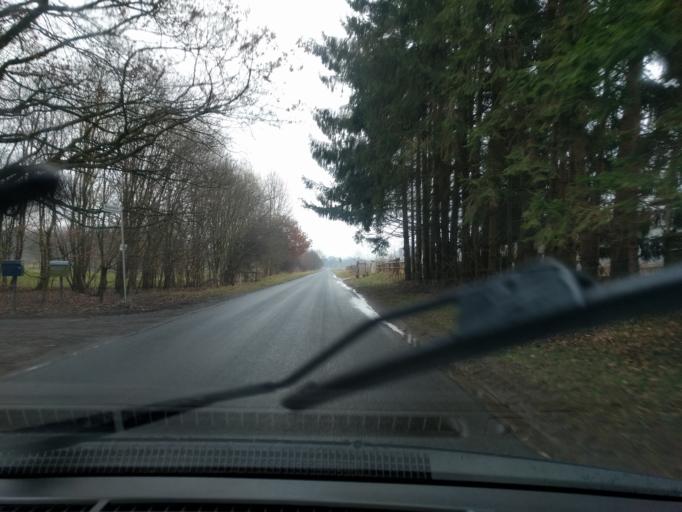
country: DE
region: Lower Saxony
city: Bendestorf
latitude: 53.3637
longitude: 9.9666
